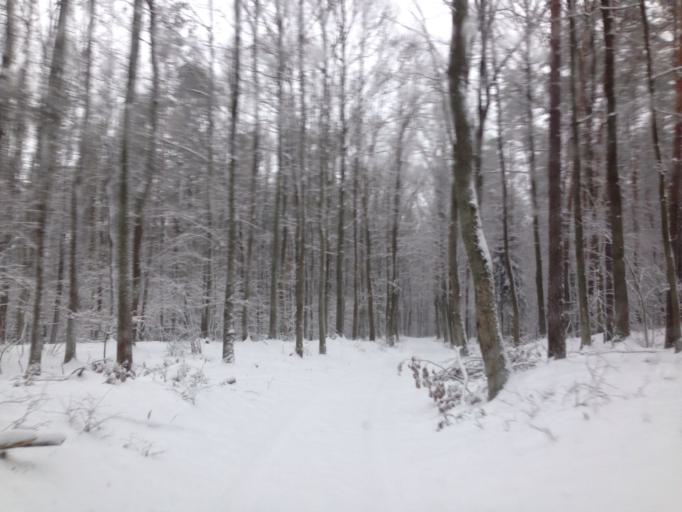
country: PL
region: Kujawsko-Pomorskie
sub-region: Powiat brodnicki
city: Gorzno
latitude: 53.1962
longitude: 19.6699
